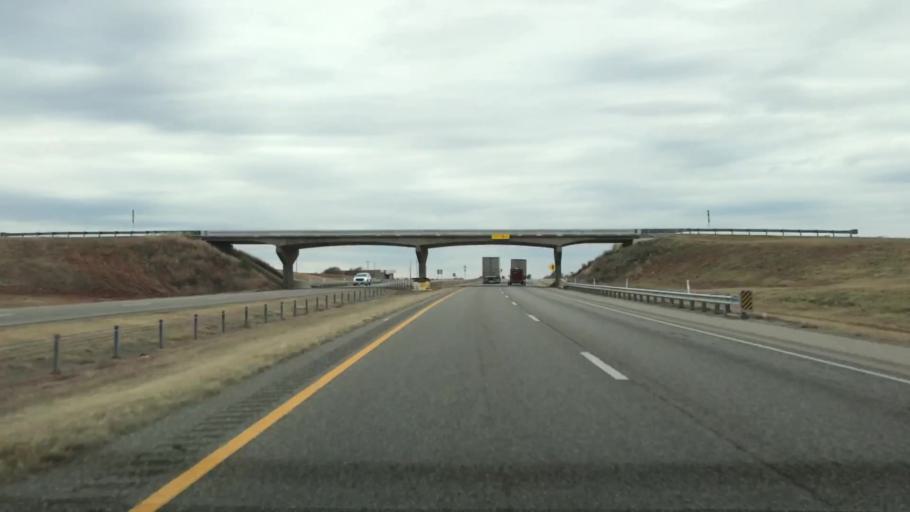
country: US
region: Oklahoma
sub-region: Custer County
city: Clinton
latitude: 35.4809
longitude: -99.0240
